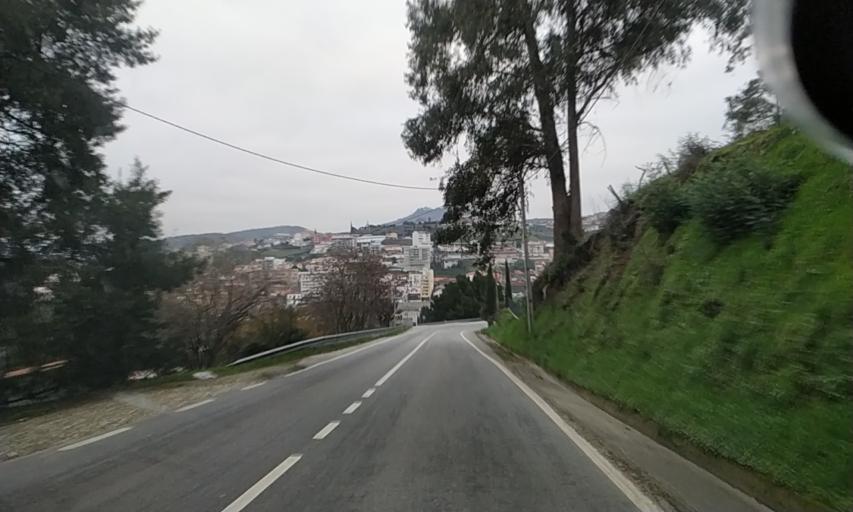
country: PT
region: Vila Real
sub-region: Peso da Regua
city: Peso da Regua
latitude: 41.1544
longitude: -7.7904
